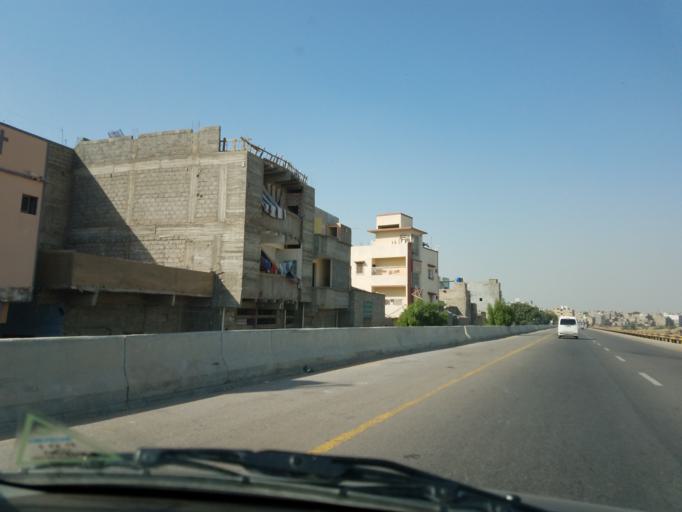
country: PK
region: Sindh
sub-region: Karachi District
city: Karachi
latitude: 24.9192
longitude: 67.0787
